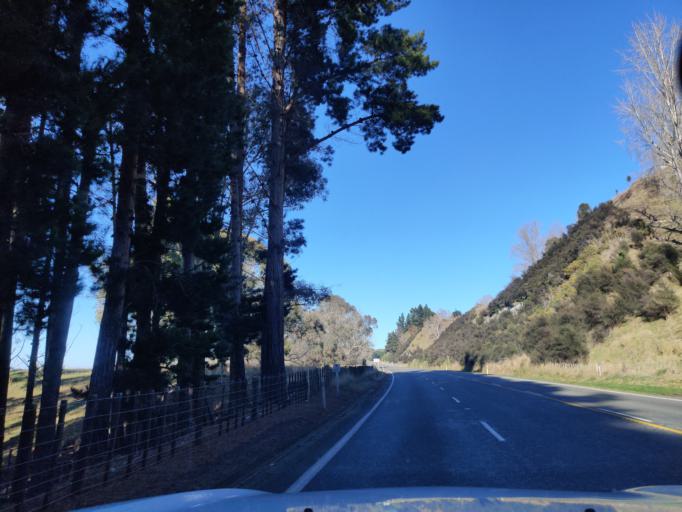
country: NZ
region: Manawatu-Wanganui
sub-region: Ruapehu District
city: Waiouru
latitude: -39.7616
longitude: 175.8043
